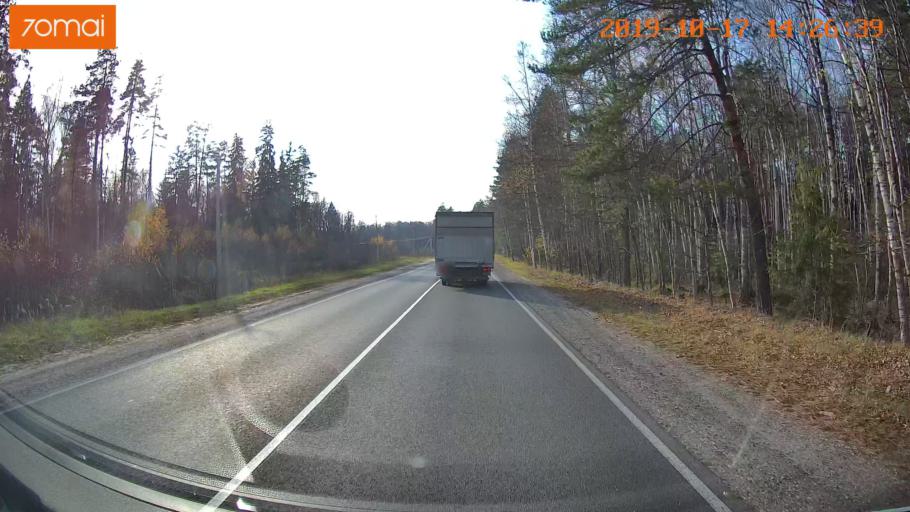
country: RU
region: Moskovskaya
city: Radovitskiy
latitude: 54.9907
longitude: 39.9641
